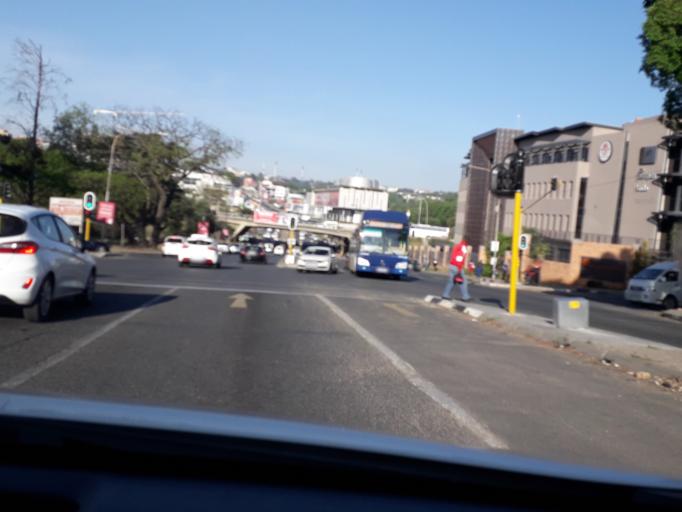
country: ZA
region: Gauteng
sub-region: City of Johannesburg Metropolitan Municipality
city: Johannesburg
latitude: -26.1281
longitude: 28.0741
